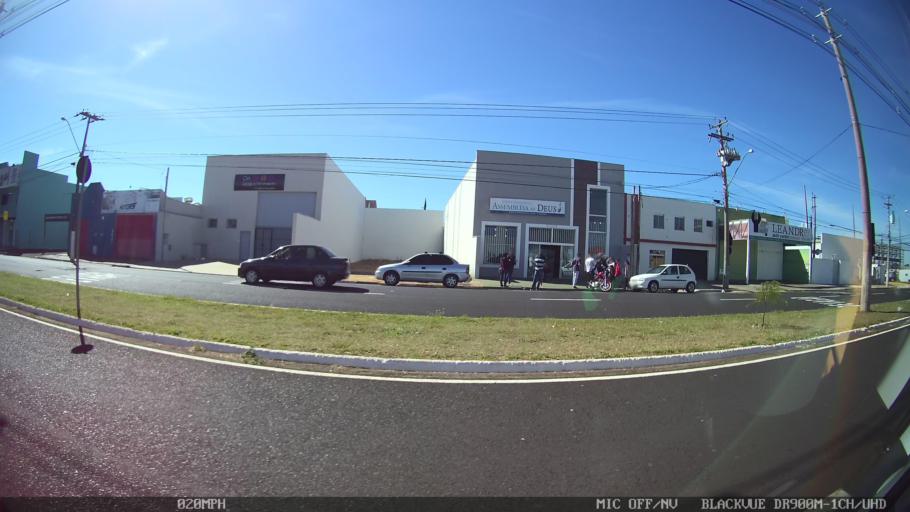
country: BR
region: Sao Paulo
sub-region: Franca
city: Franca
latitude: -20.5455
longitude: -47.3743
